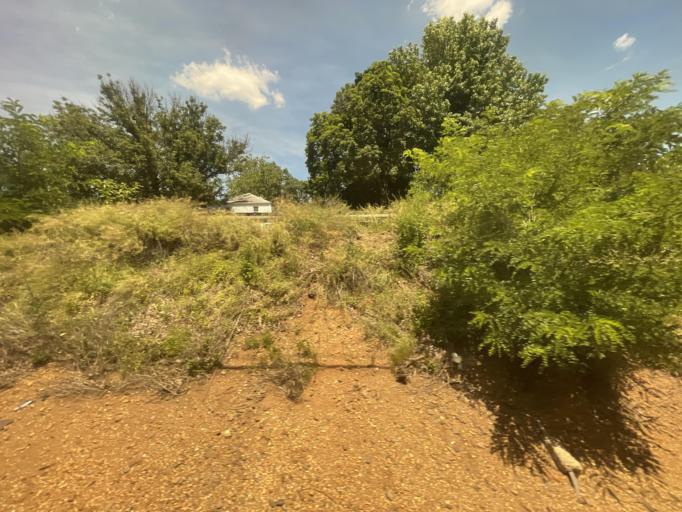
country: US
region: New Jersey
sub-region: Middlesex County
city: Metuchen
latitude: 40.5415
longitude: -74.3588
